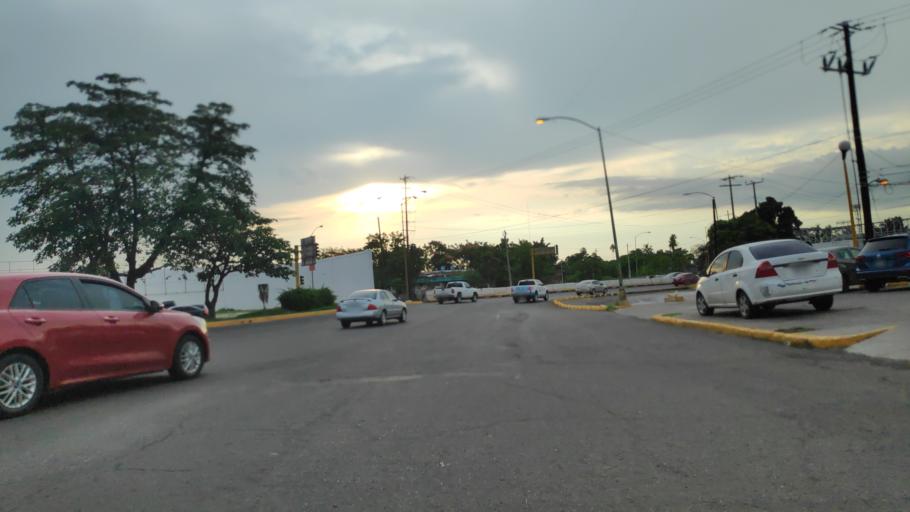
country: MX
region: Sinaloa
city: Culiacan
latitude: 24.8046
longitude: -107.4051
